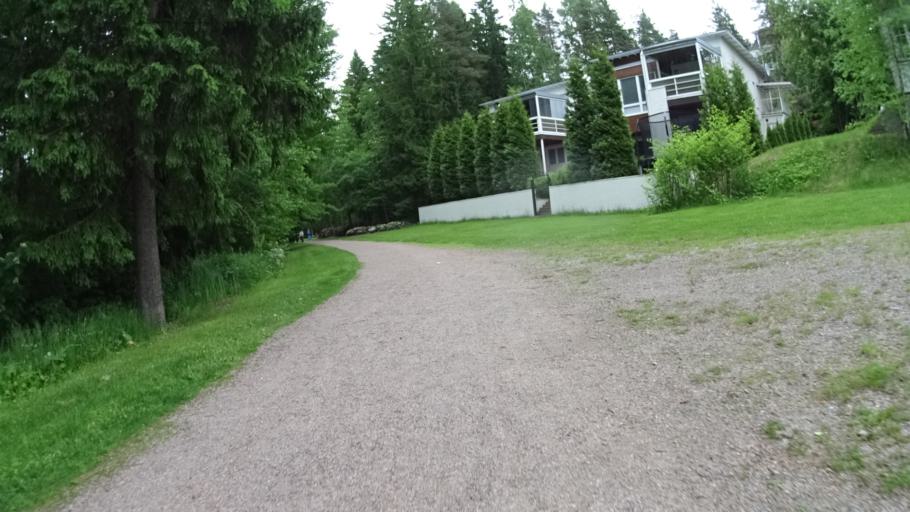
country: FI
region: Uusimaa
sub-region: Helsinki
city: Teekkarikylae
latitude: 60.2840
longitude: 24.8549
